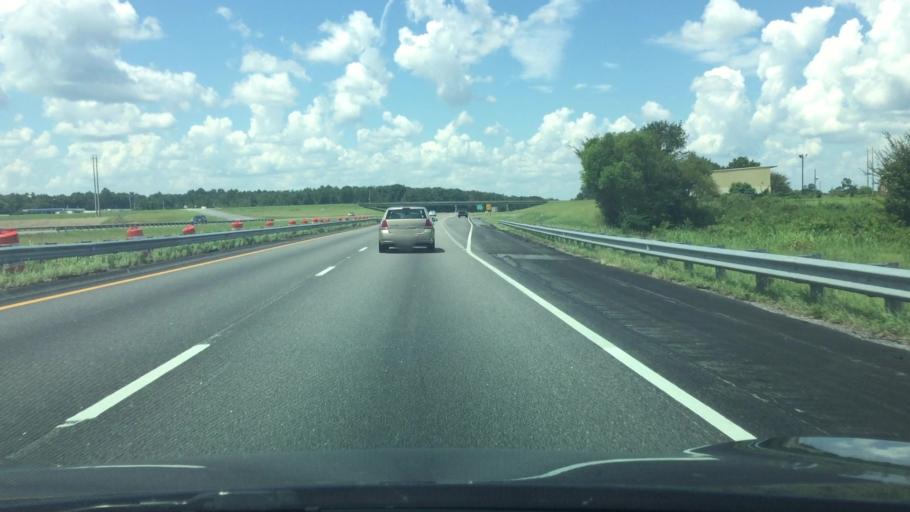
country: US
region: Alabama
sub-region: Elmore County
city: Tallassee
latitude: 32.4297
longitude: -85.8938
